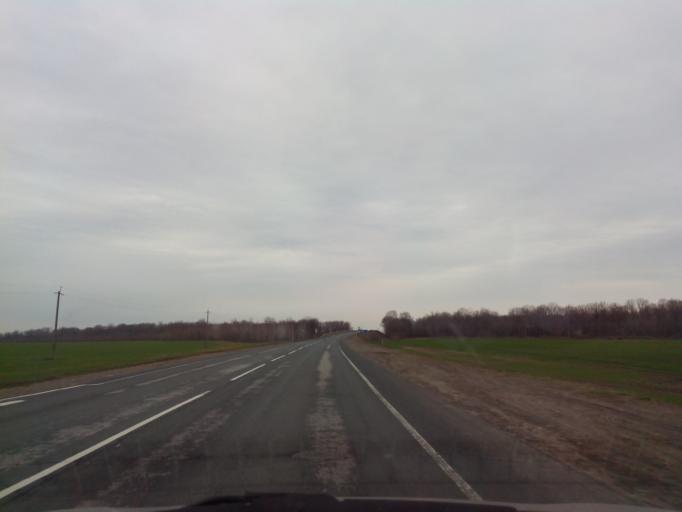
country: RU
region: Tambov
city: Zavoronezhskoye
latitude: 52.9122
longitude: 40.6308
